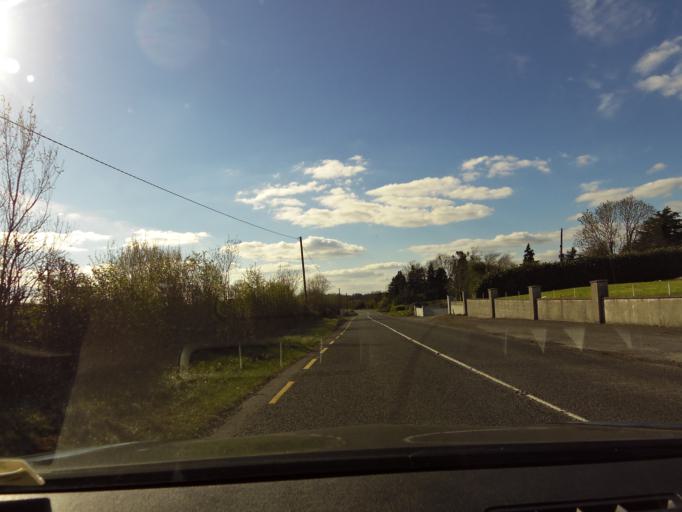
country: IE
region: Leinster
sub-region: Uibh Fhaili
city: Banagher
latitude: 53.1049
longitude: -8.0243
